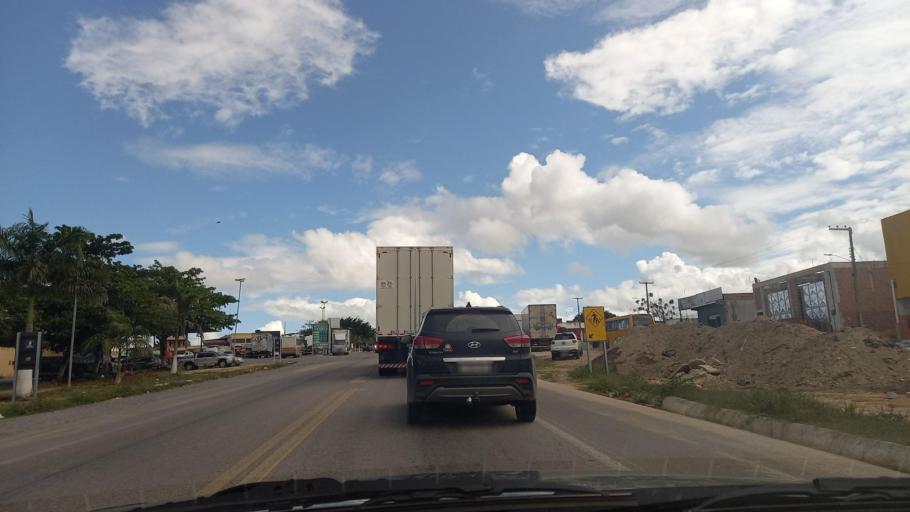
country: BR
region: Pernambuco
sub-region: Lajedo
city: Lajedo
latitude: -8.7092
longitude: -36.4190
